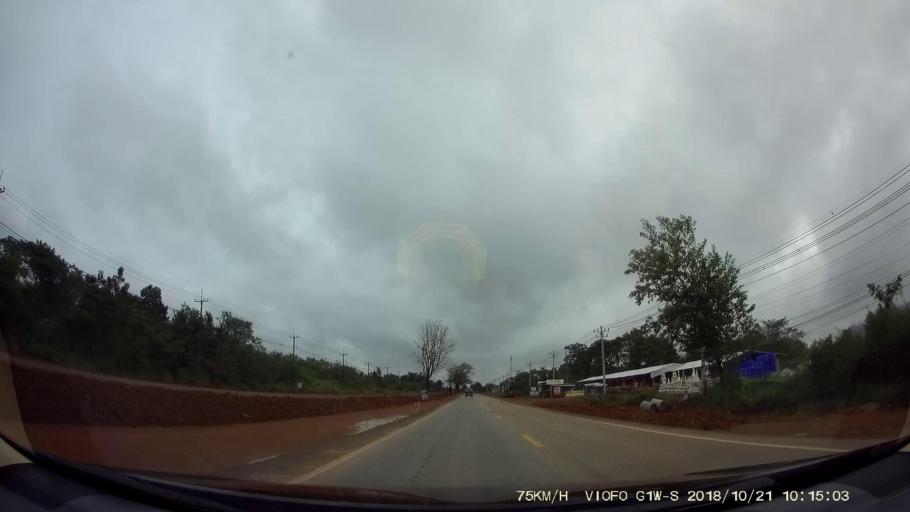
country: TH
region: Chaiyaphum
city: Phu Khiao
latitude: 16.3440
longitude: 102.1620
